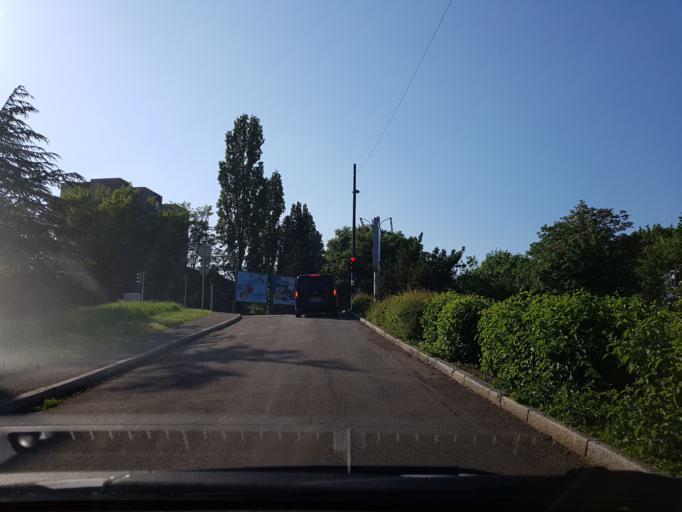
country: FR
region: Alsace
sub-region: Departement du Haut-Rhin
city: Riedisheim
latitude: 47.7553
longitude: 7.3608
